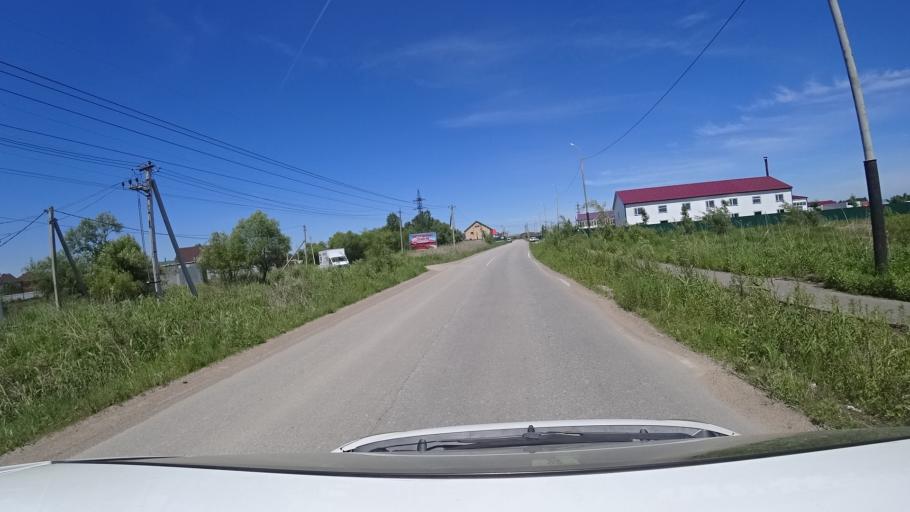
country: RU
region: Khabarovsk Krai
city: Topolevo
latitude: 48.4986
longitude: 135.1836
